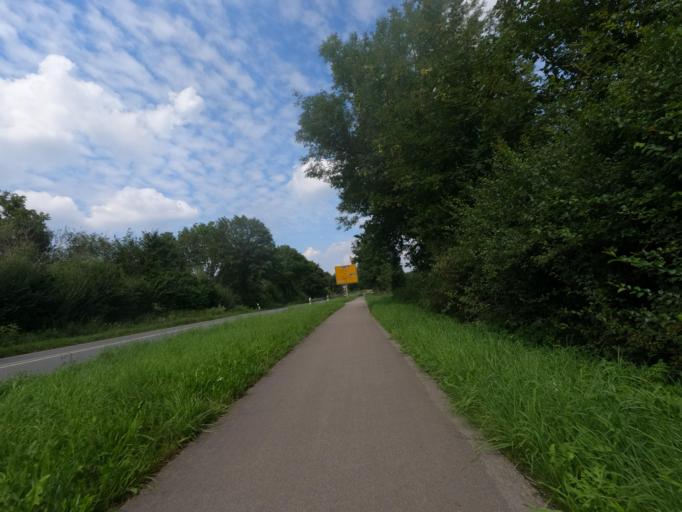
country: DE
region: North Rhine-Westphalia
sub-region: Regierungsbezirk Koln
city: Ubach-Palenberg
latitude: 50.9497
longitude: 6.1302
